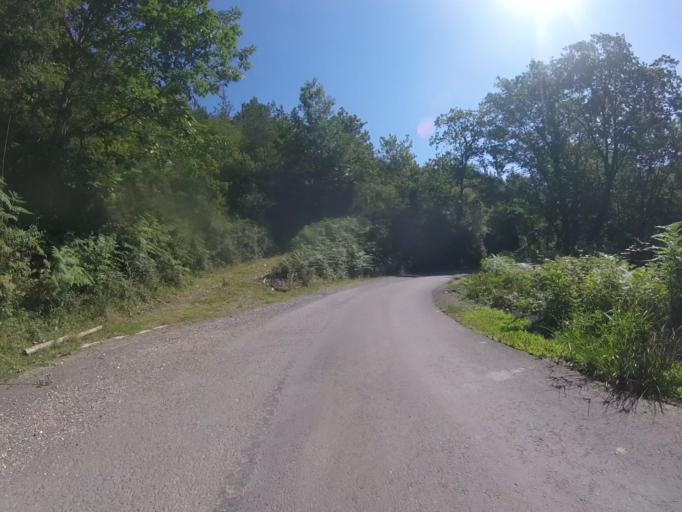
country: ES
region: Navarre
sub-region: Provincia de Navarra
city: Goizueta
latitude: 43.1867
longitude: -1.8357
